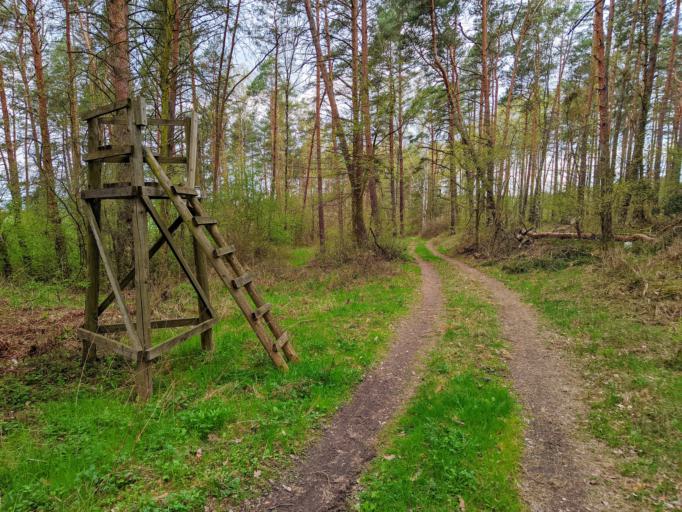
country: PL
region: Lubusz
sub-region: Powiat swiebodzinski
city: Lubrza
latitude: 52.3851
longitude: 15.4819
